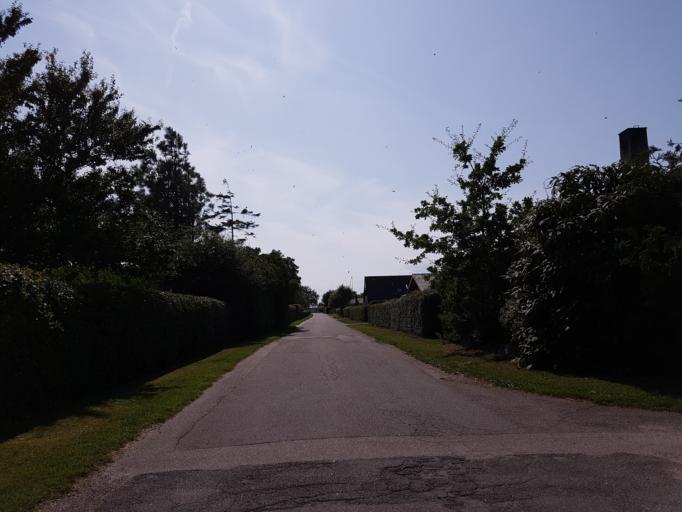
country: DK
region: Zealand
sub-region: Guldborgsund Kommune
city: Nykobing Falster
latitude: 54.5728
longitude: 11.9371
